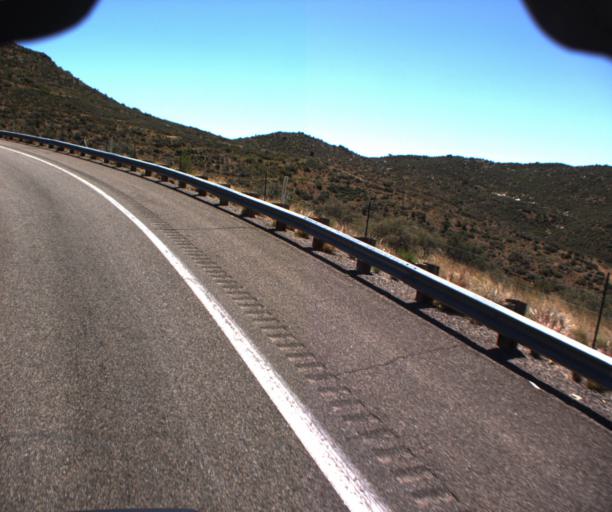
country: US
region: Arizona
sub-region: Yavapai County
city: Congress
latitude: 34.2058
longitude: -112.7560
